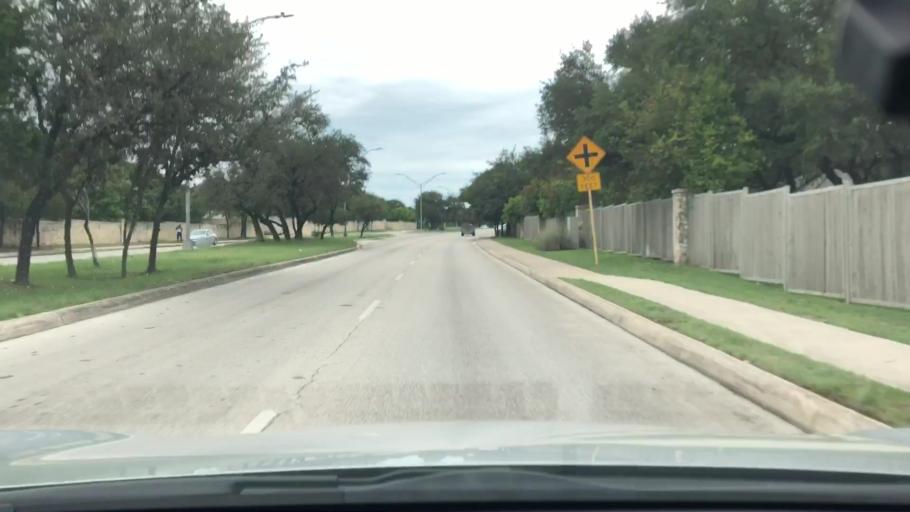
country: US
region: Texas
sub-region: Bexar County
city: Leon Valley
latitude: 29.4605
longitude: -98.6722
